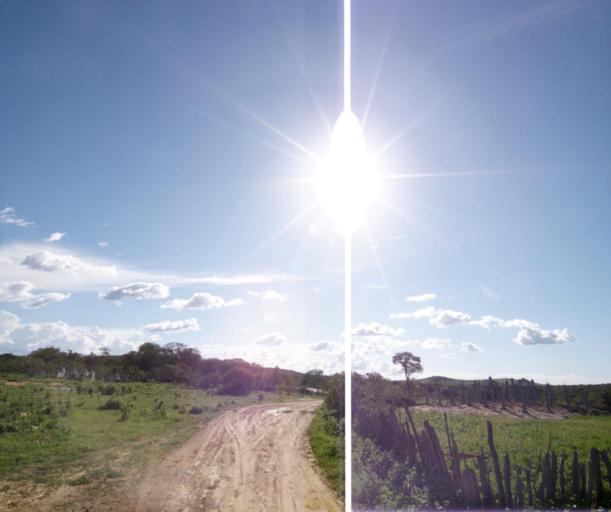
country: BR
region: Bahia
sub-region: Tanhacu
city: Tanhacu
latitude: -14.1867
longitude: -40.9479
